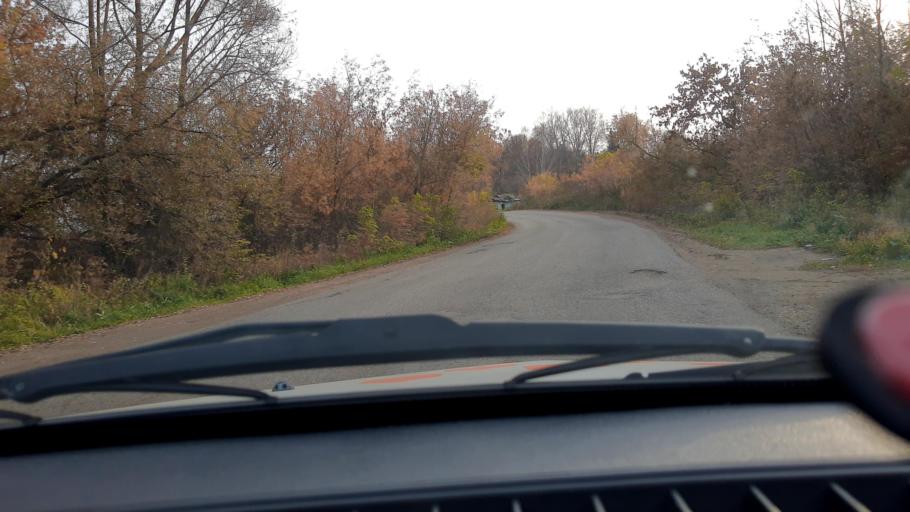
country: RU
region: Bashkortostan
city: Iglino
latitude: 54.7993
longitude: 56.3142
